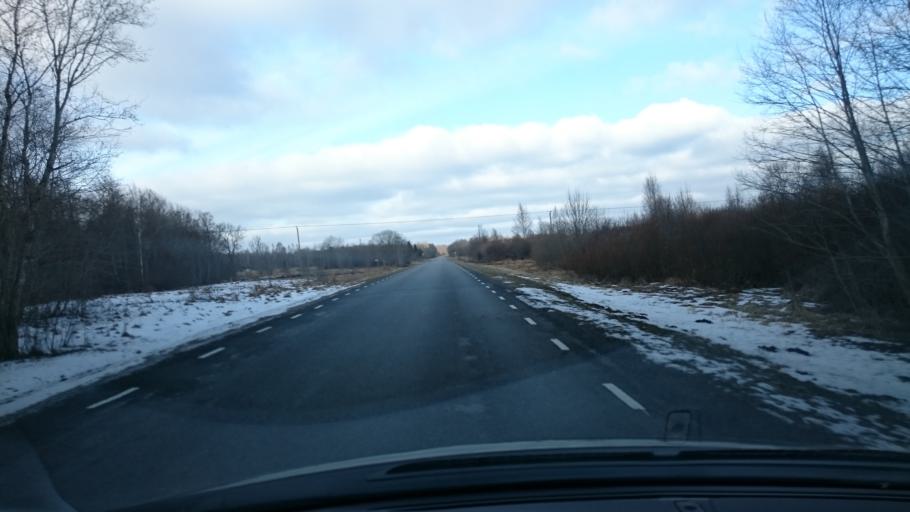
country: EE
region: Harju
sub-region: Keila linn
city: Keila
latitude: 59.3733
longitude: 24.3130
